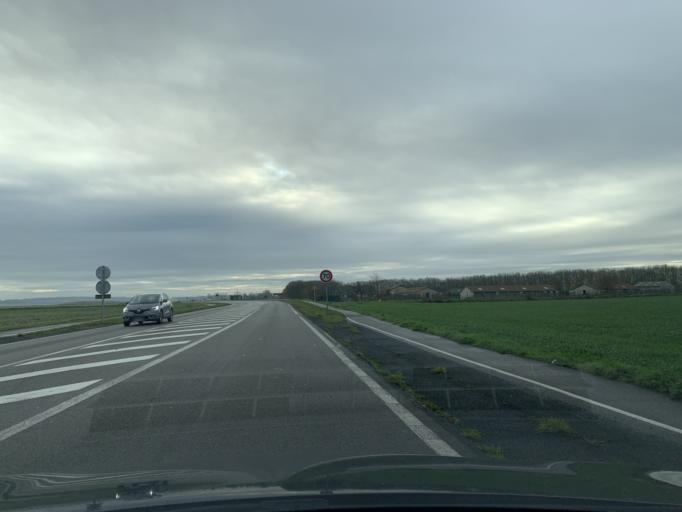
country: FR
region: Nord-Pas-de-Calais
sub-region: Departement du Nord
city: Goeulzin
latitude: 50.3319
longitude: 3.1046
